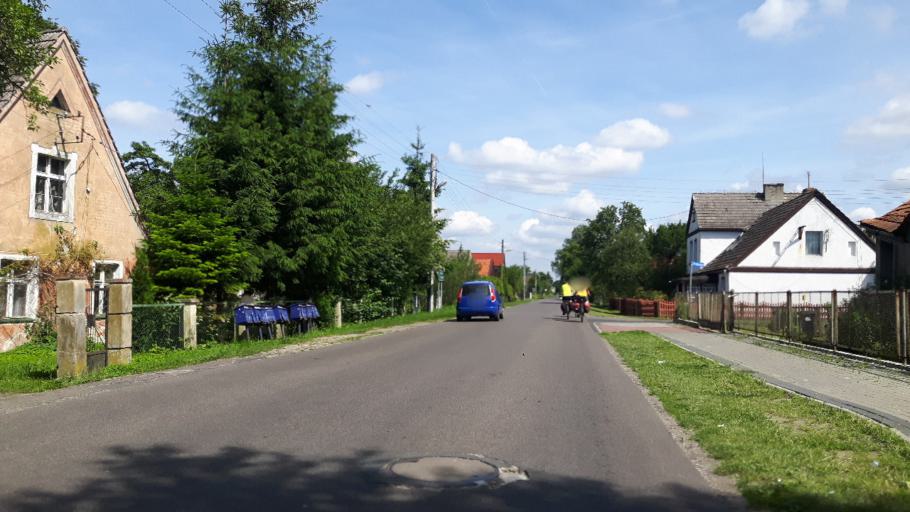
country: PL
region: West Pomeranian Voivodeship
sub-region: Powiat goleniowski
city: Goleniow
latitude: 53.4882
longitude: 14.7768
